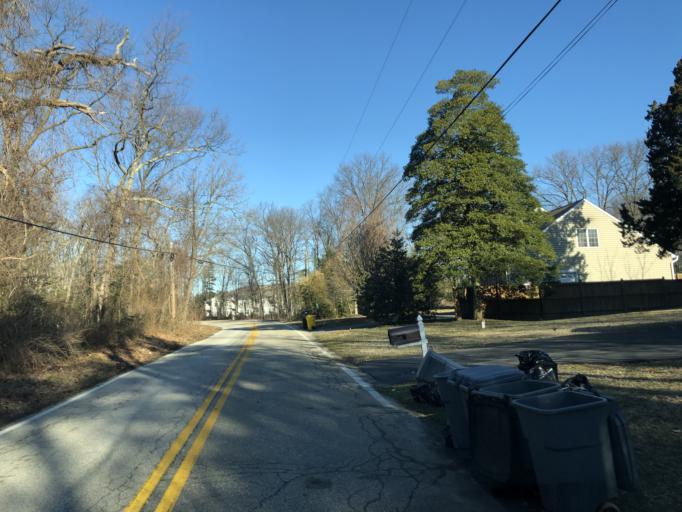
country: US
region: Maryland
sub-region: Anne Arundel County
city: Pasadena
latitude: 39.1296
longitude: -76.5772
